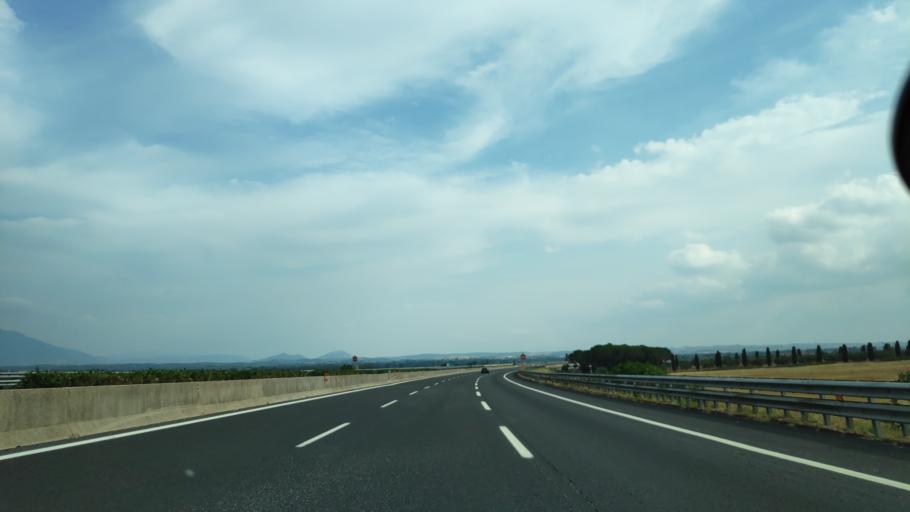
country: IT
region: Latium
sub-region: Citta metropolitana di Roma Capitale
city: Fiano Romano
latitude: 42.1565
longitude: 12.6236
